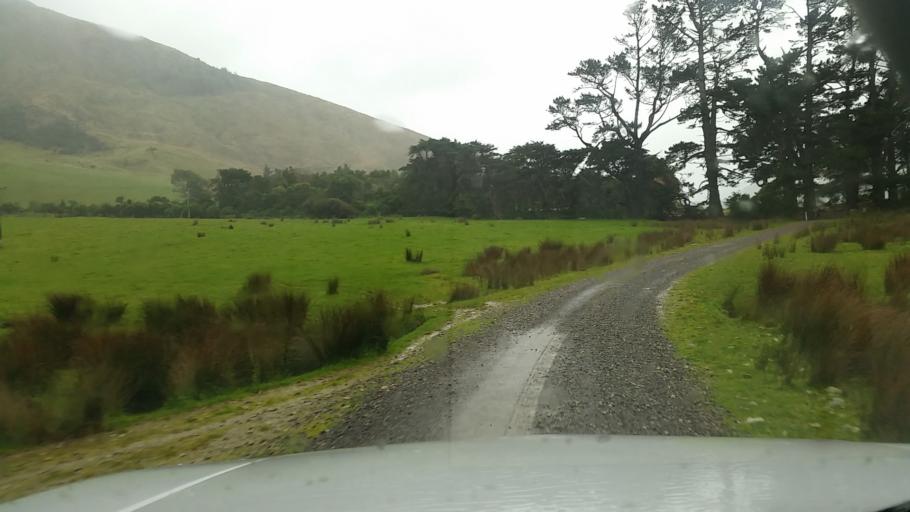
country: NZ
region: Marlborough
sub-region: Marlborough District
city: Picton
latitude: -41.1148
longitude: 174.0354
